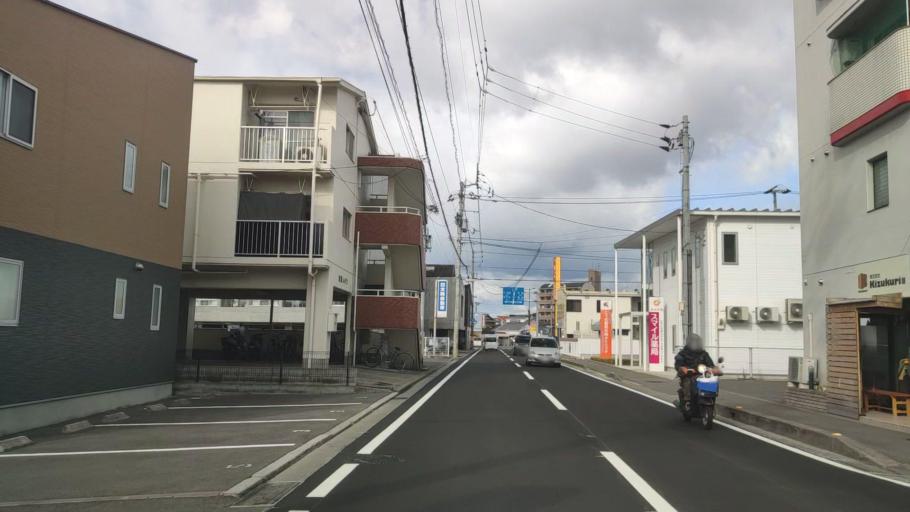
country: JP
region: Ehime
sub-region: Shikoku-chuo Shi
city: Matsuyama
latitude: 33.8224
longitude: 132.7582
